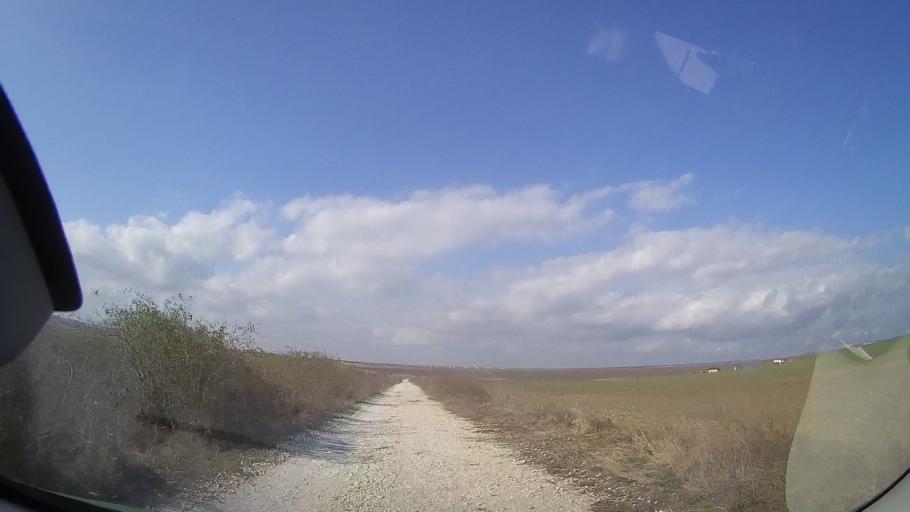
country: RO
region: Constanta
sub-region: Comuna Douazeci si Trei August
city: Douazeci si Trei August
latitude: 43.9053
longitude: 28.6158
